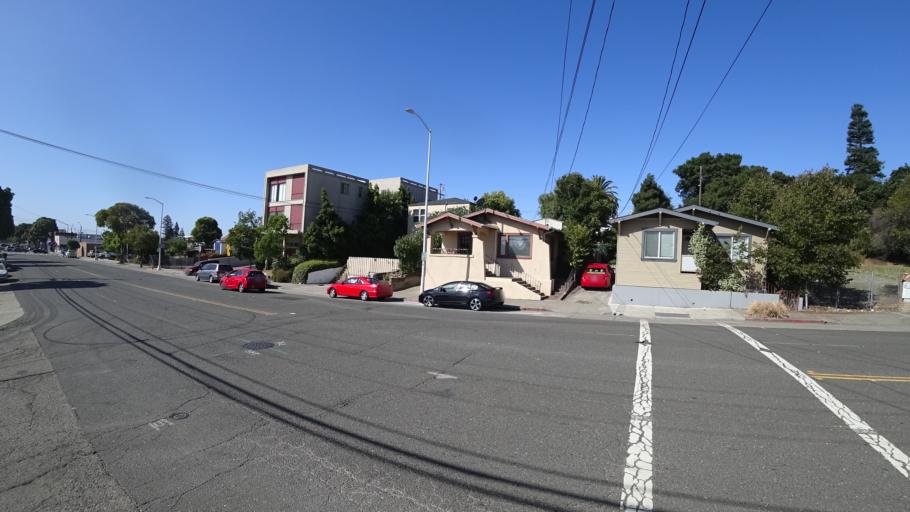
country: US
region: California
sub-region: Alameda County
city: Hayward
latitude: 37.6751
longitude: -122.0848
